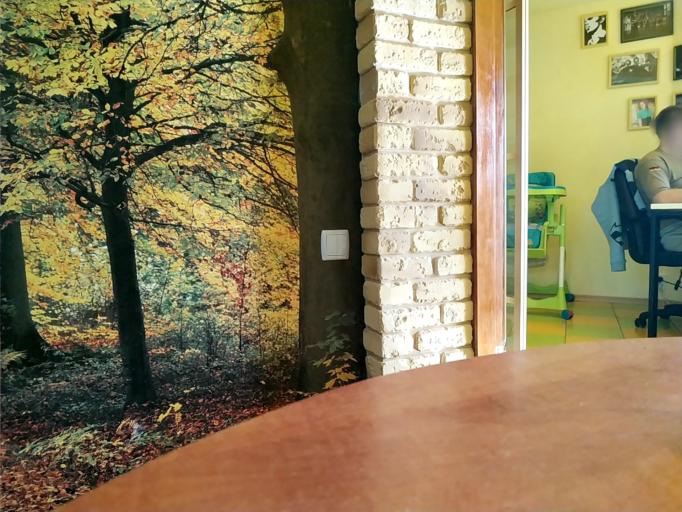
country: RU
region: Tverskaya
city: Vasil'yevskiy Mokh
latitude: 57.1929
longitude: 35.7587
